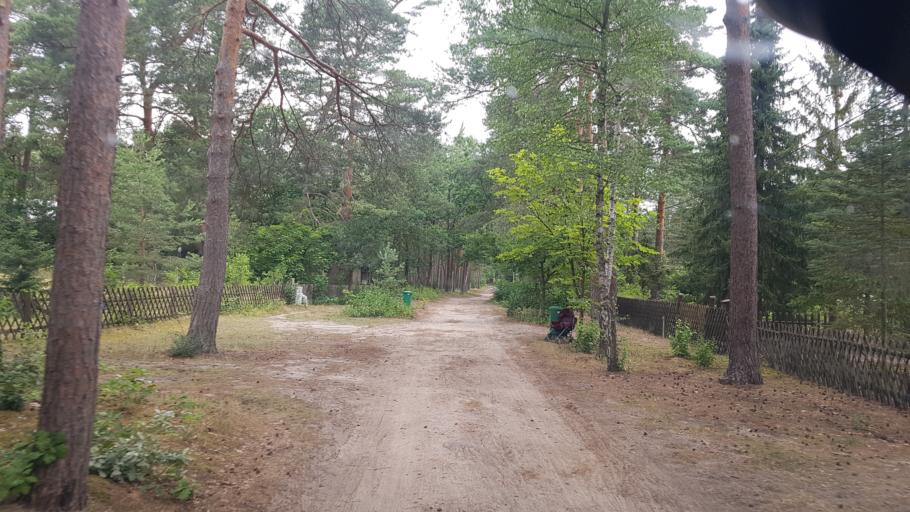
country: DE
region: Brandenburg
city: Gross Koris
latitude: 52.1603
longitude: 13.6971
